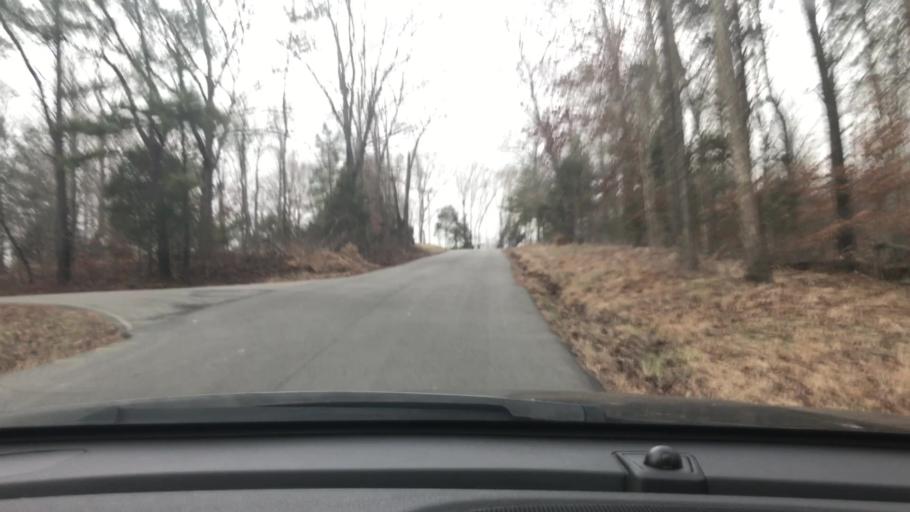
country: US
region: Tennessee
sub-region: Dickson County
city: Charlotte
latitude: 36.1804
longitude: -87.2794
